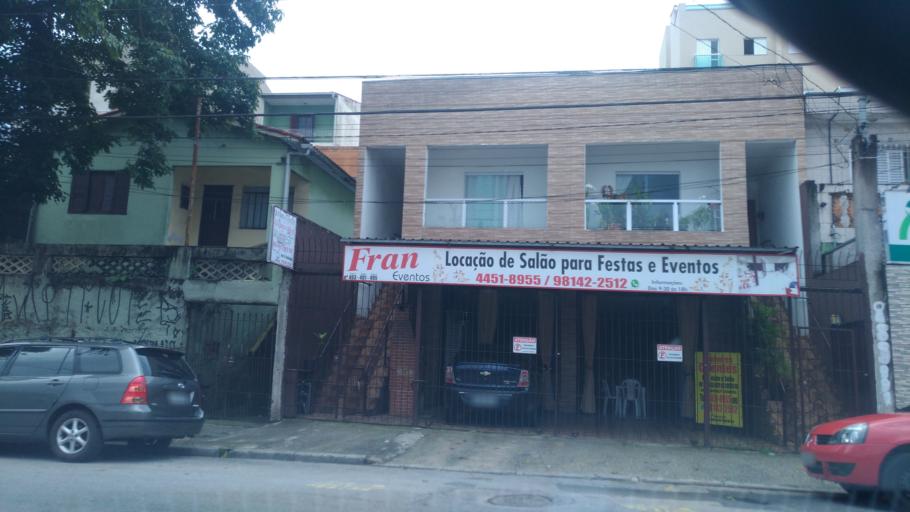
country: BR
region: Sao Paulo
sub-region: Santo Andre
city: Santo Andre
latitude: -23.7025
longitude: -46.5037
